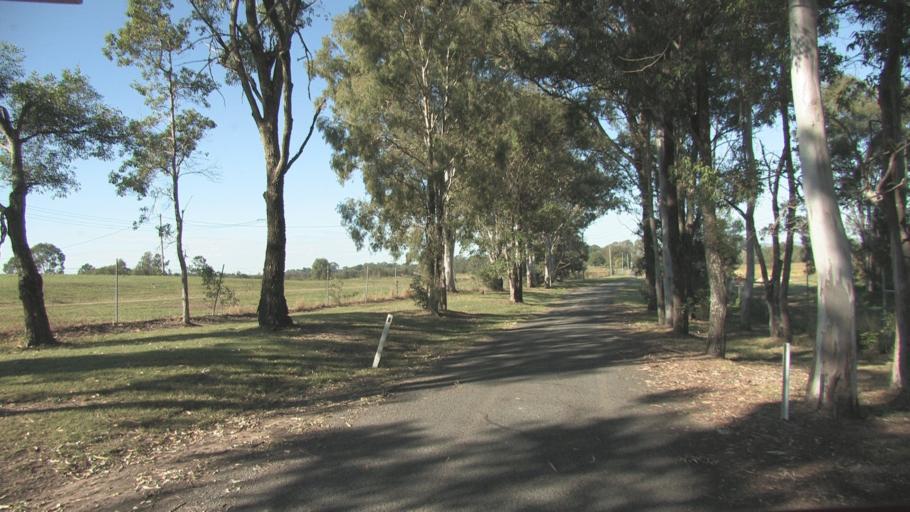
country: AU
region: Queensland
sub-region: Gold Coast
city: Yatala
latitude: -27.6907
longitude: 153.2797
